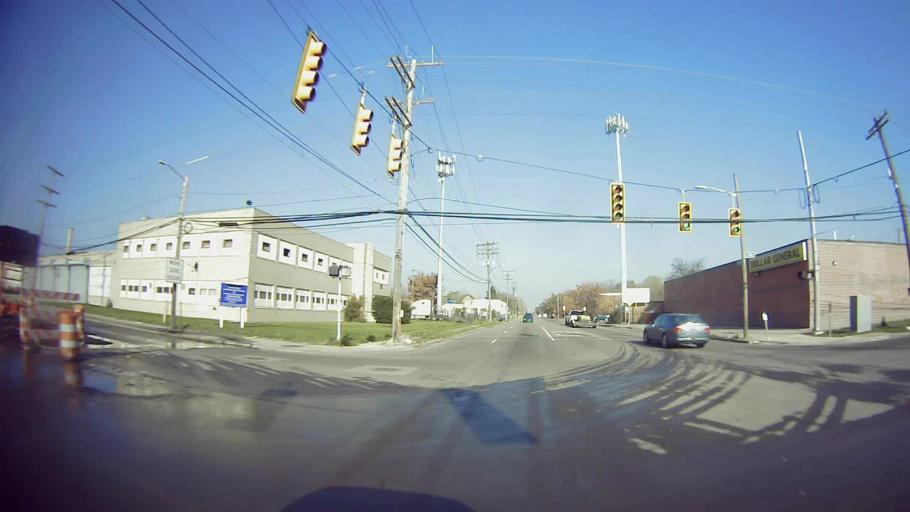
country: US
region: Michigan
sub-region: Wayne County
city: Dearborn
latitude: 42.3588
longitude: -83.1775
